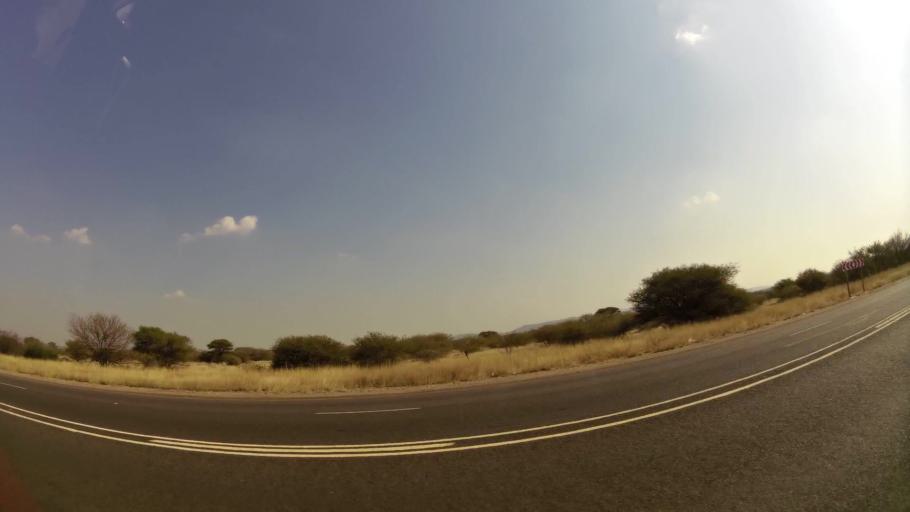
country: ZA
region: North-West
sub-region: Bojanala Platinum District Municipality
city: Mogwase
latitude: -25.3994
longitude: 27.0728
